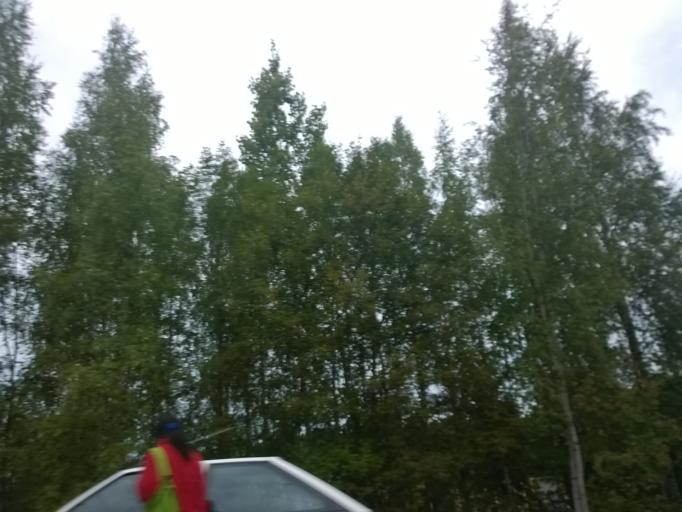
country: FI
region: Pirkanmaa
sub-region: Tampere
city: Tampere
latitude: 61.4578
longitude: 23.8432
